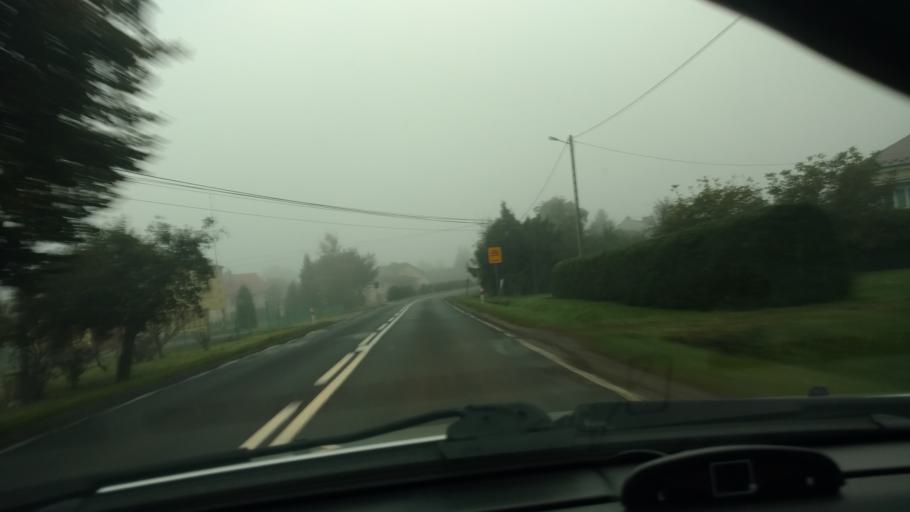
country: PL
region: Subcarpathian Voivodeship
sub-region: Powiat strzyzowski
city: Wisniowa
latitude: 49.8717
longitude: 21.6865
